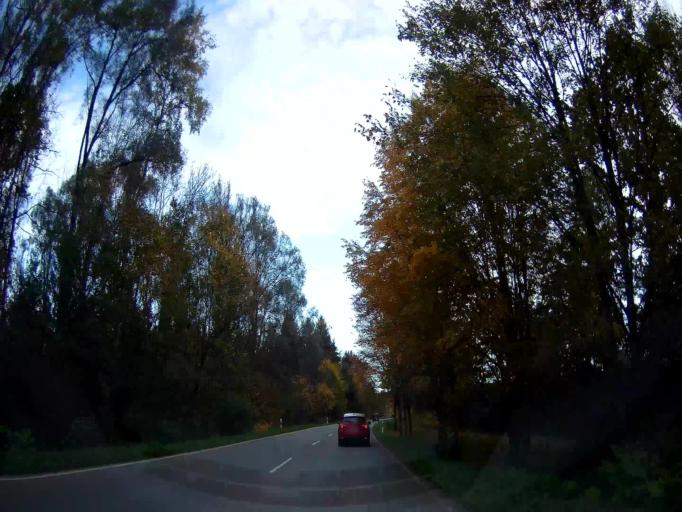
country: DE
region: Bavaria
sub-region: Upper Bavaria
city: Piding
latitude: 47.7575
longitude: 12.9204
